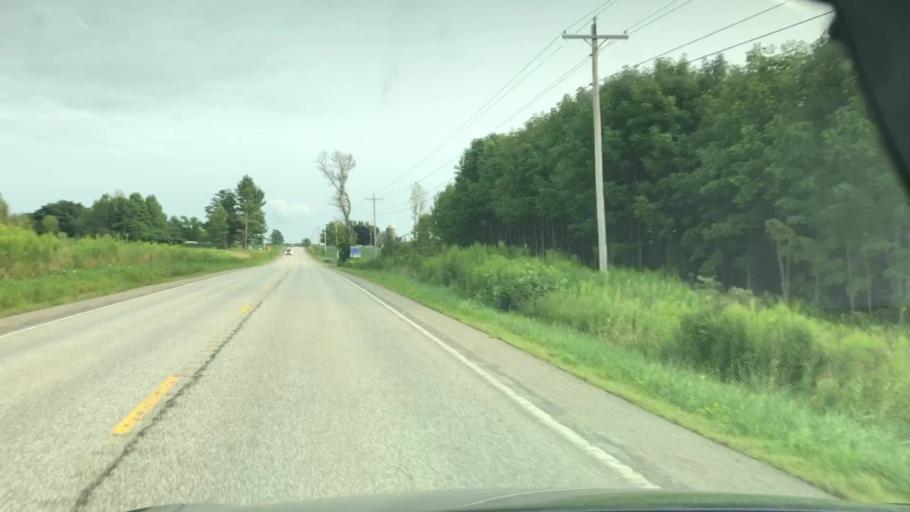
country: US
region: Pennsylvania
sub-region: Erie County
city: Union City
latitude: 41.8639
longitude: -79.8334
